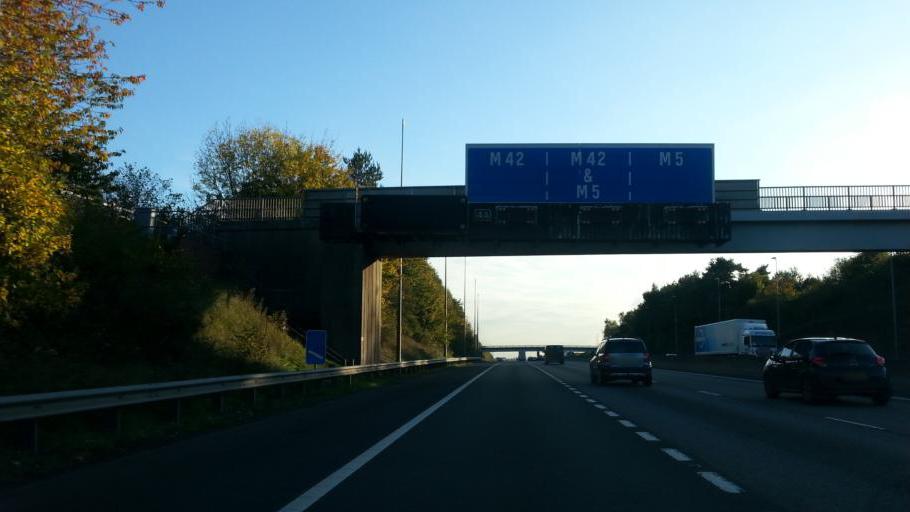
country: GB
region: England
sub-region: Worcestershire
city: Bromsgrove
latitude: 52.3627
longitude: -2.0682
